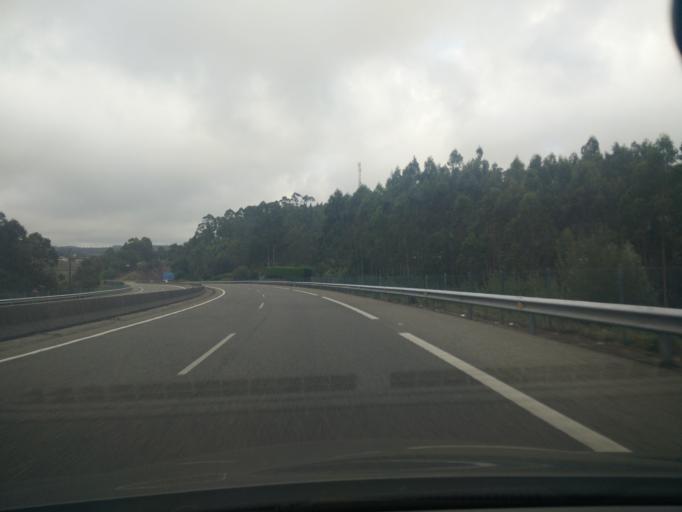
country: ES
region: Galicia
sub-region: Provincia da Coruna
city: Laracha
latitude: 43.2682
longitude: -8.5639
